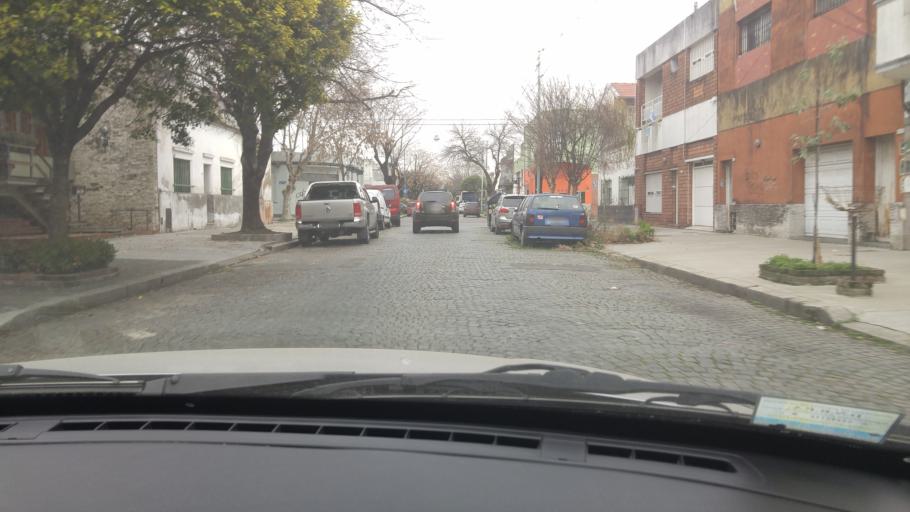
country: AR
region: Buenos Aires F.D.
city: Villa Santa Rita
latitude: -34.6329
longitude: -58.4923
